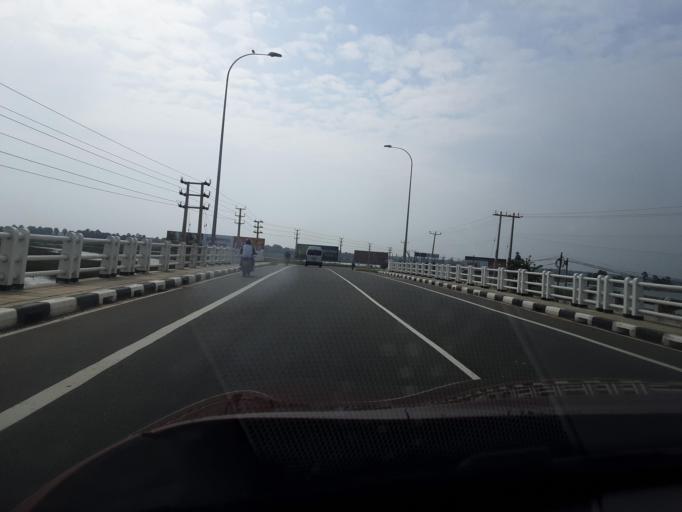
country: LK
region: Northern Province
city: Jaffna
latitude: 9.6642
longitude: 80.0701
